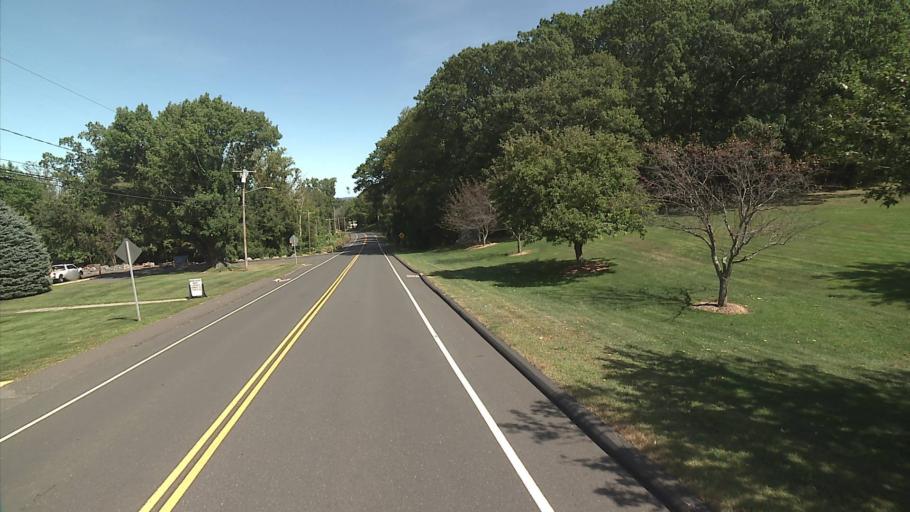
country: US
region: Connecticut
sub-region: New Haven County
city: Middlebury
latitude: 41.5277
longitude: -73.1213
